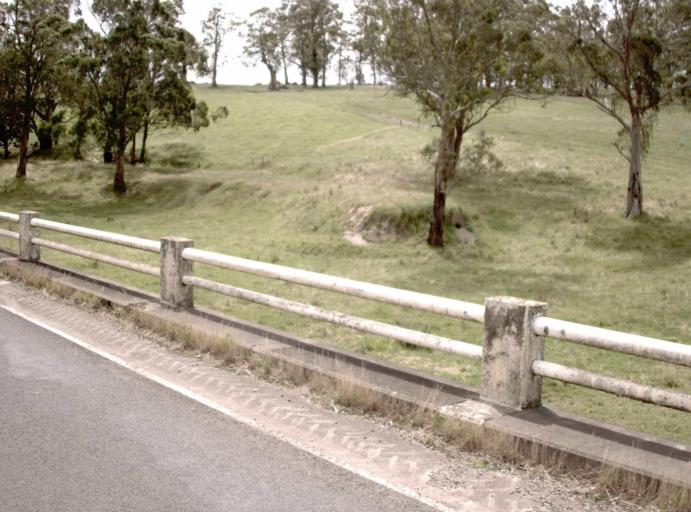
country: AU
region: Victoria
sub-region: Latrobe
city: Moe
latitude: -38.0877
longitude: 146.1610
